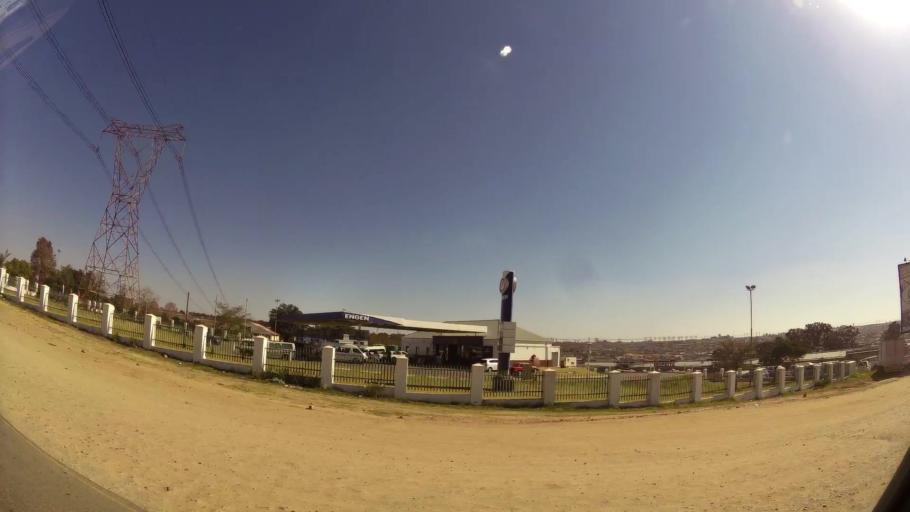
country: ZA
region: Gauteng
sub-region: City of Johannesburg Metropolitan Municipality
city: Midrand
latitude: -25.9258
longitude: 28.0980
